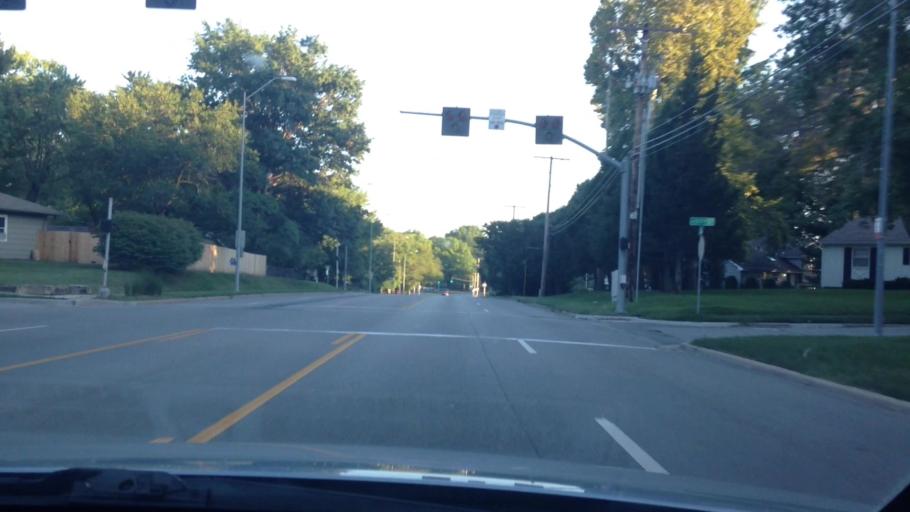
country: US
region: Kansas
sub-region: Johnson County
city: Leawood
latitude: 38.9295
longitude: -94.5941
